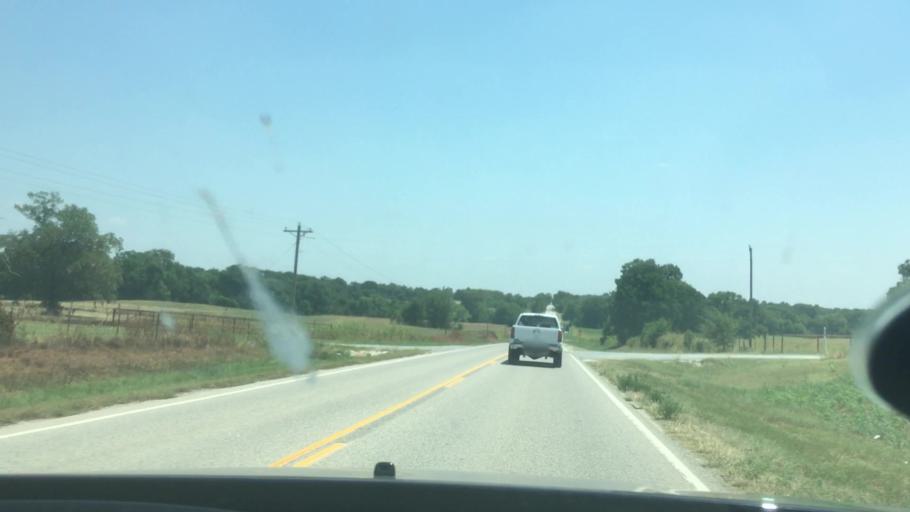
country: US
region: Oklahoma
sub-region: Bryan County
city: Durant
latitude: 34.1730
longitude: -96.4122
